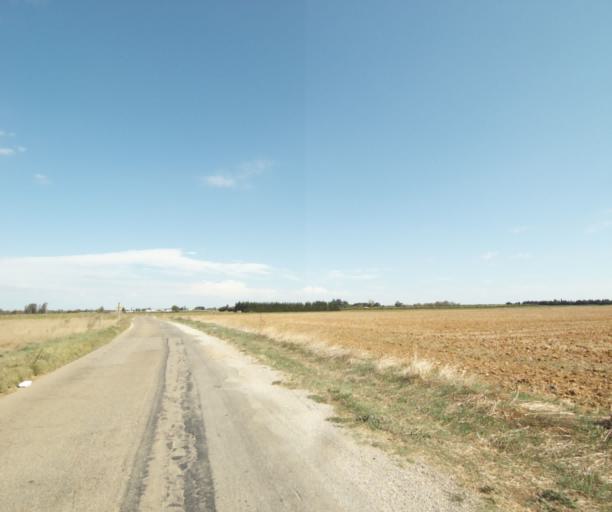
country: FR
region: Languedoc-Roussillon
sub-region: Departement du Gard
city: Bouillargues
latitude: 43.8001
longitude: 4.4482
